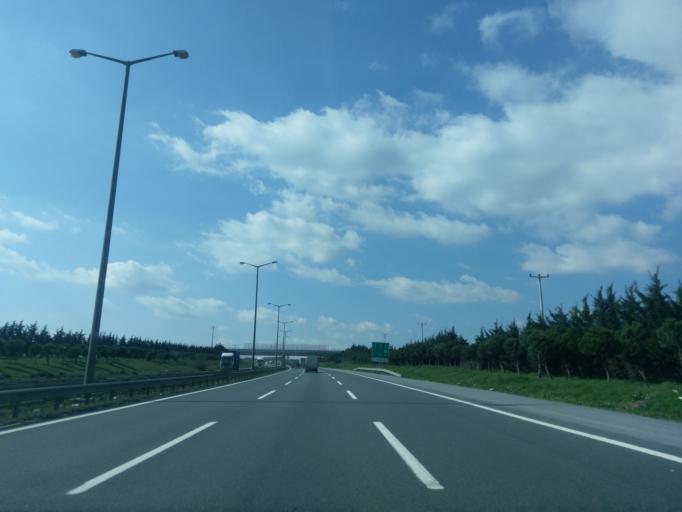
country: TR
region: Istanbul
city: Silivri
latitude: 41.1228
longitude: 28.2394
